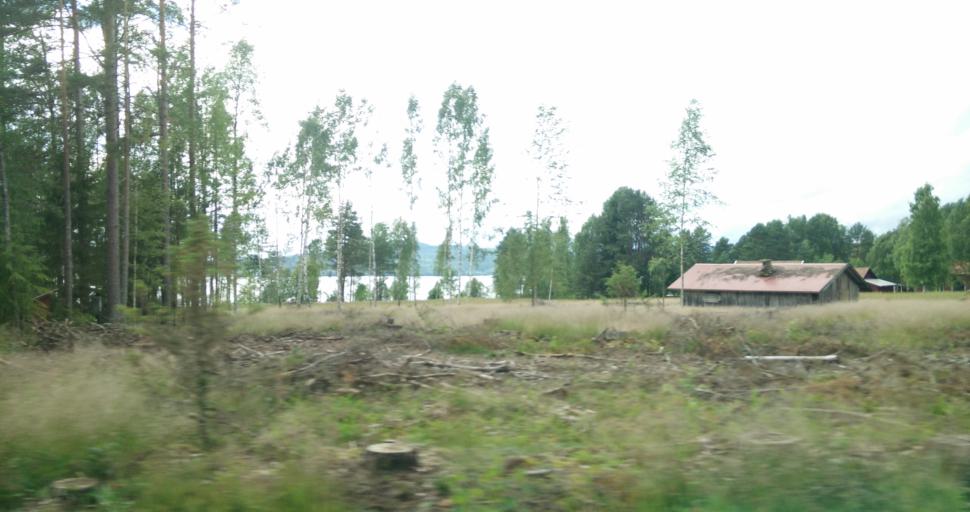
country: SE
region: Vaermland
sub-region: Munkfors Kommun
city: Munkfors
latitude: 59.9791
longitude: 13.4873
